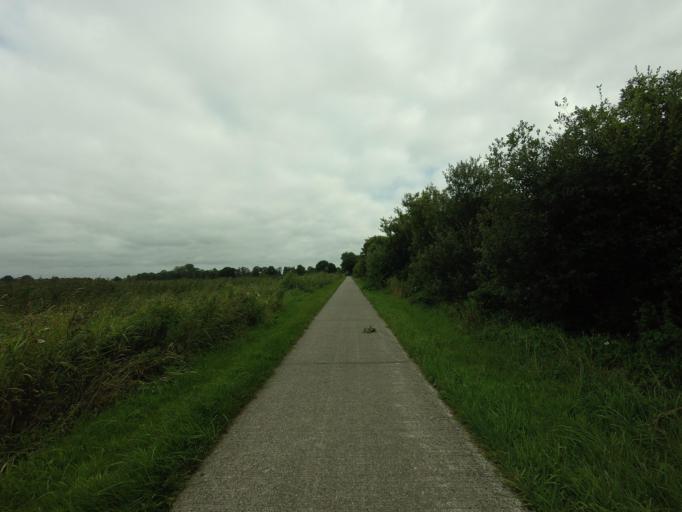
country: NL
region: Overijssel
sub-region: Gemeente Steenwijkerland
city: Giethoorn
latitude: 52.7107
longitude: 6.0685
